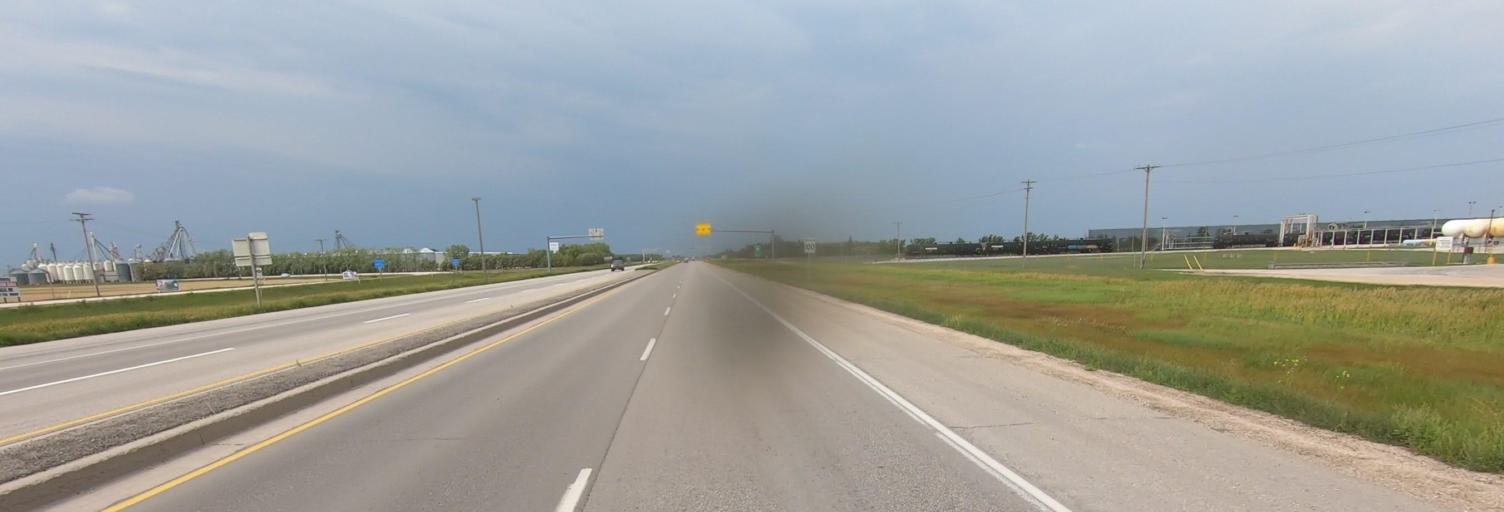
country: CA
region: Manitoba
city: Winnipeg
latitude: 49.7682
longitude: -97.2319
